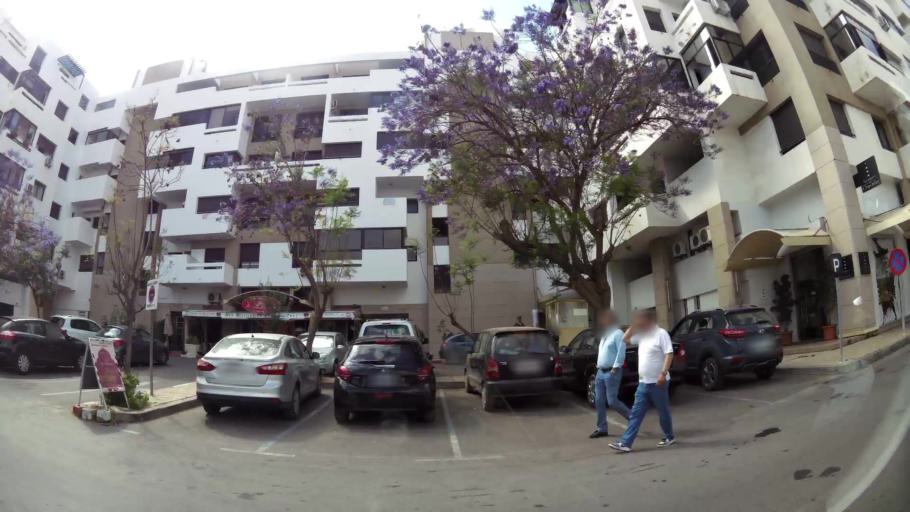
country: MA
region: Rabat-Sale-Zemmour-Zaer
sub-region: Skhirate-Temara
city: Temara
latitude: 33.9607
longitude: -6.8668
